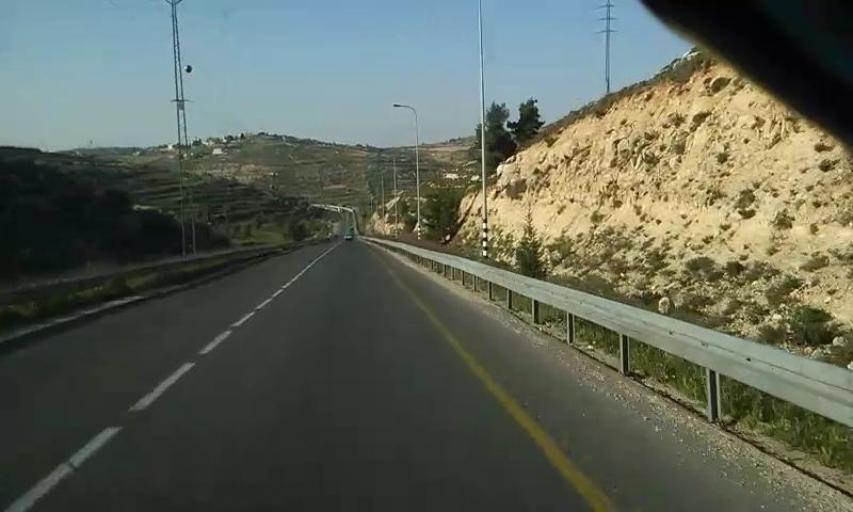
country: PS
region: West Bank
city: Halhul
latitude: 31.5899
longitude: 35.1161
